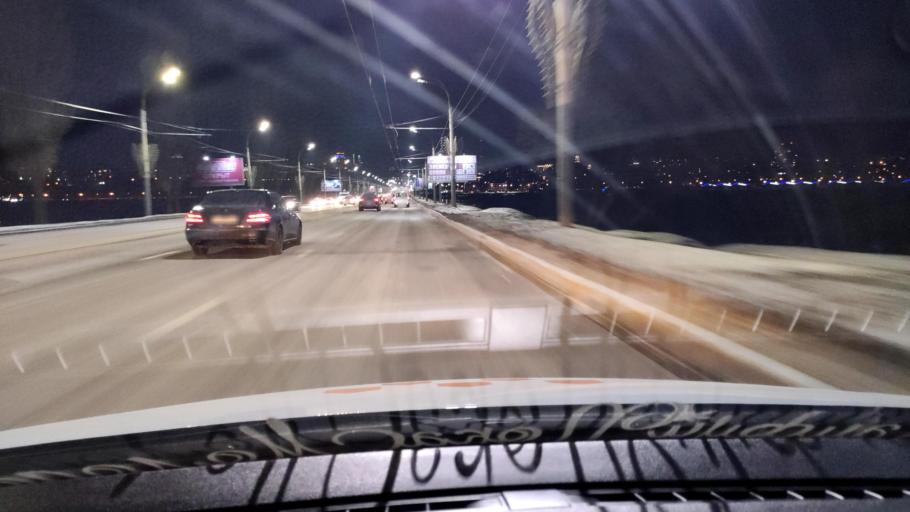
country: RU
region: Voronezj
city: Voronezh
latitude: 51.6653
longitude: 39.2407
